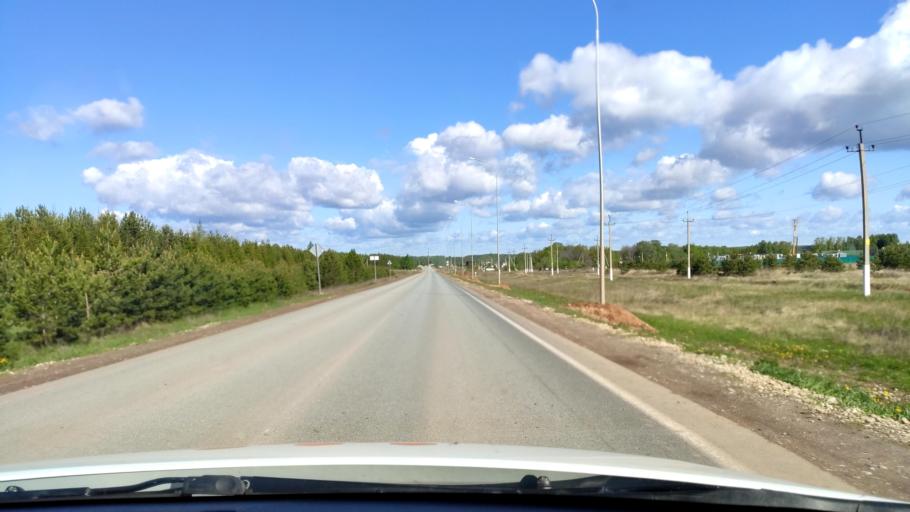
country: RU
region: Tatarstan
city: Sviyazhsk
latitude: 55.7429
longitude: 48.7305
